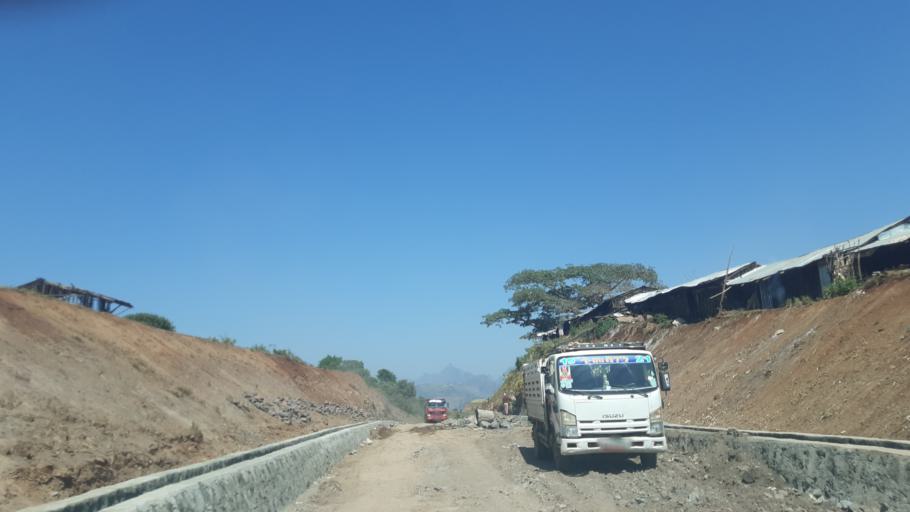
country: ET
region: Amhara
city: Dabat
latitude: 13.1628
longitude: 37.6064
